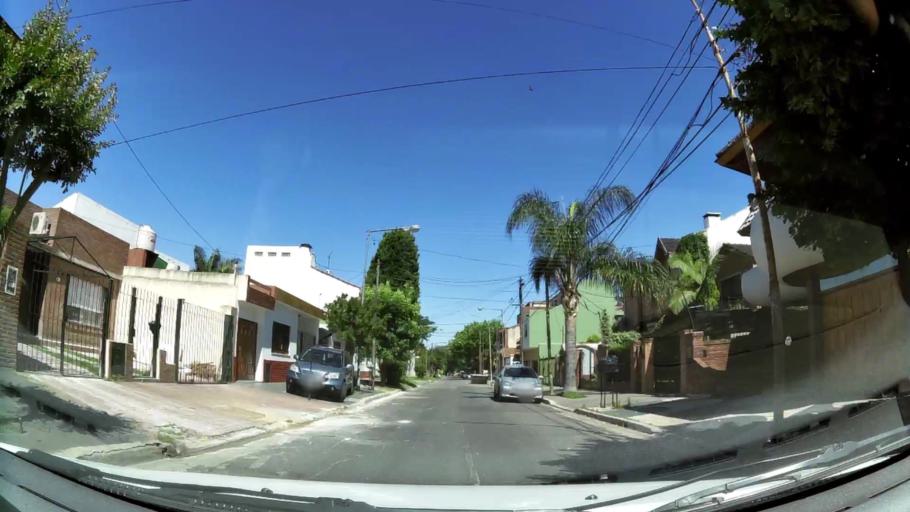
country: AR
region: Buenos Aires
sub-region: Partido de General San Martin
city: General San Martin
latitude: -34.5574
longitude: -58.5572
